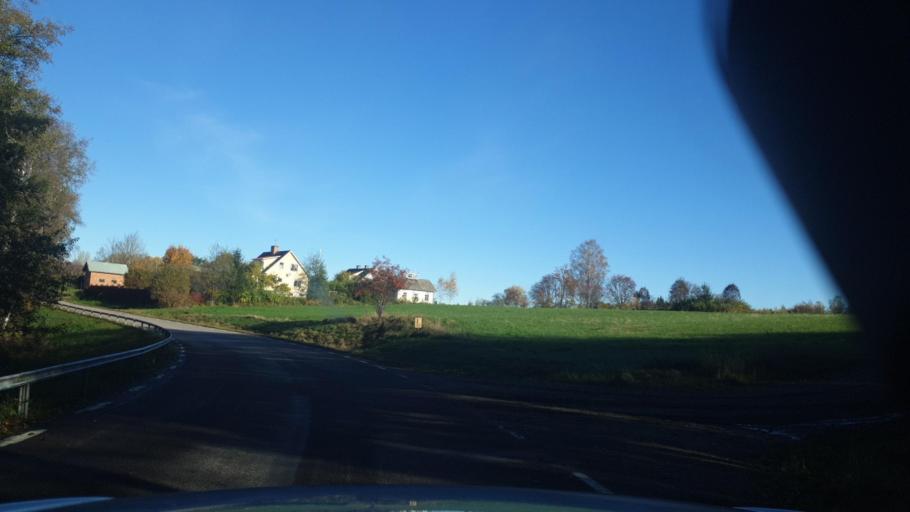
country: SE
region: Vaermland
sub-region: Arvika Kommun
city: Arvika
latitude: 59.5917
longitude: 12.7537
